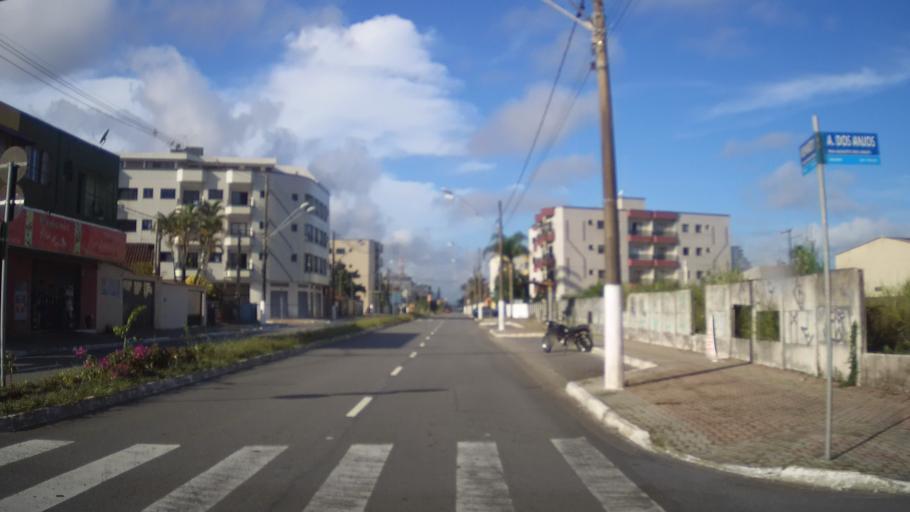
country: BR
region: Sao Paulo
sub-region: Mongagua
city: Mongagua
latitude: -24.0819
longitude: -46.5956
